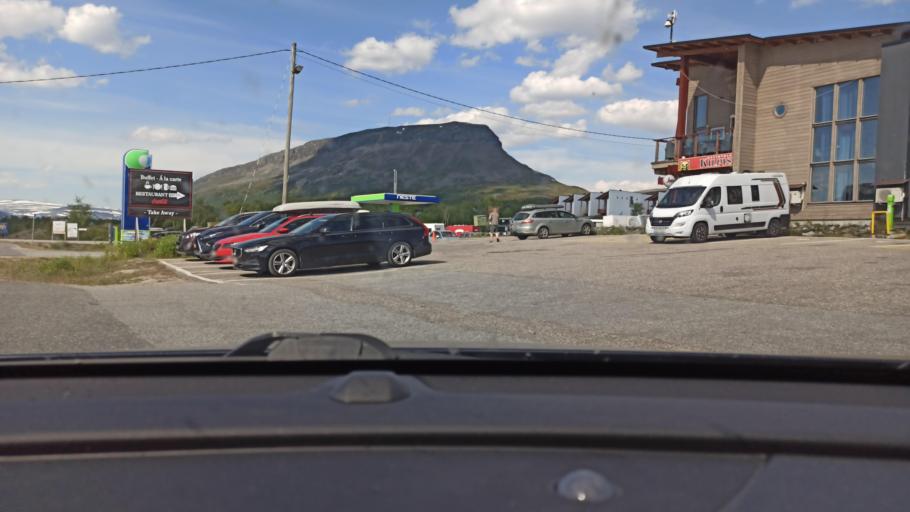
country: NO
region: Troms
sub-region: Kafjord
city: Olderdalen
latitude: 69.0164
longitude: 20.8755
